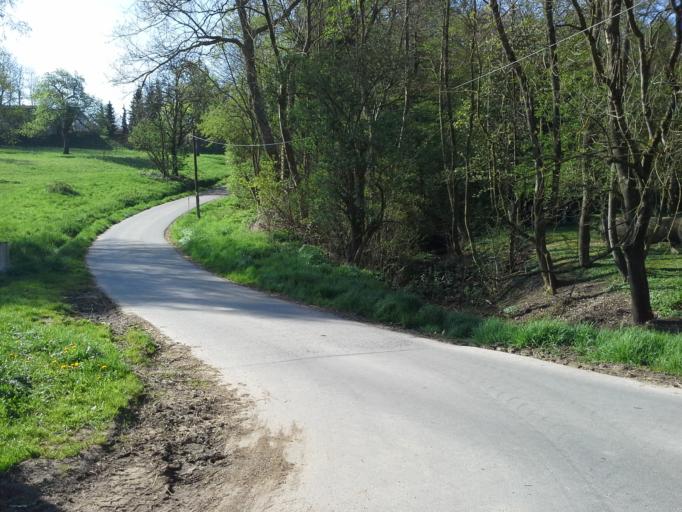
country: DE
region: Baden-Wuerttemberg
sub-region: Karlsruhe Region
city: Neuenburg
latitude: 48.8924
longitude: 8.5791
